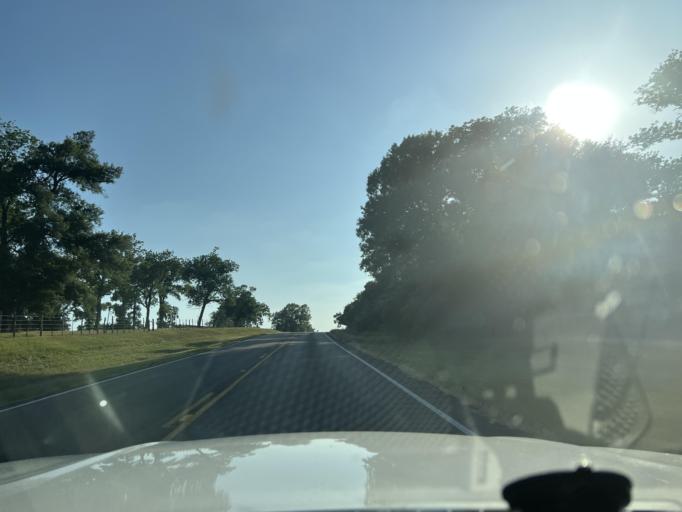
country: US
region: Texas
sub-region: Washington County
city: Brenham
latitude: 30.2371
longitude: -96.2643
